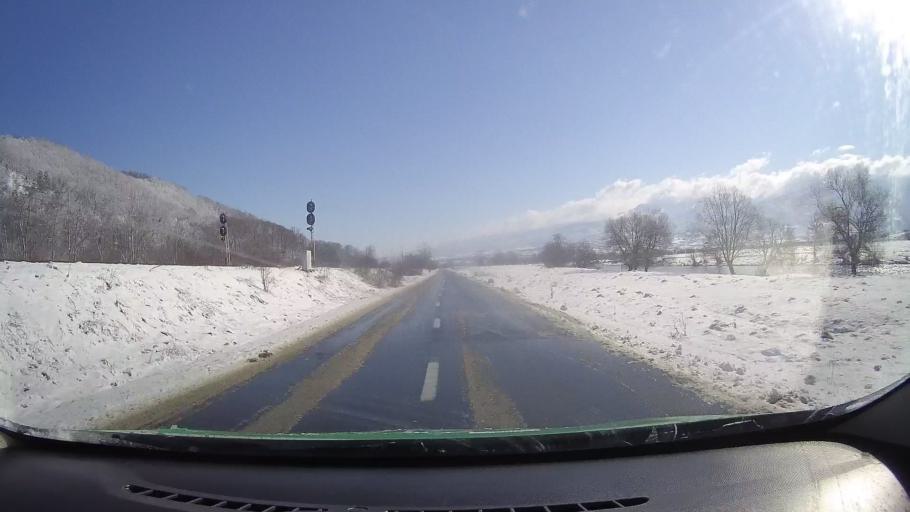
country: RO
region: Sibiu
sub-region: Comuna Talmaciu
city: Talmaciu
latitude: 45.6617
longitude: 24.2852
